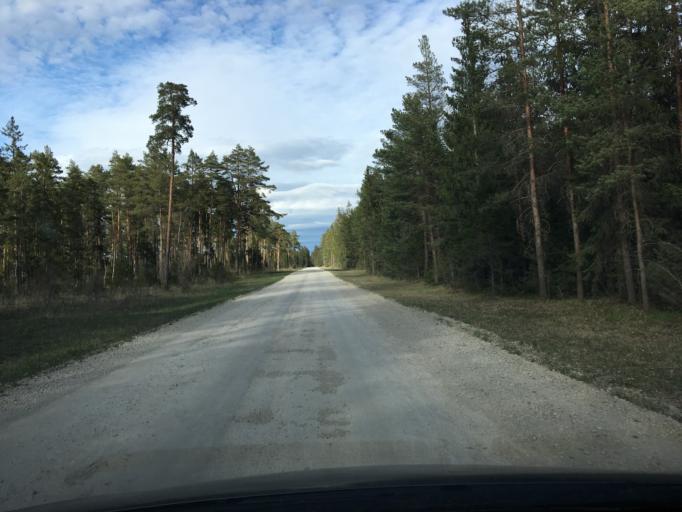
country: EE
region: Raplamaa
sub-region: Maerjamaa vald
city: Marjamaa
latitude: 59.0153
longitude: 24.4170
